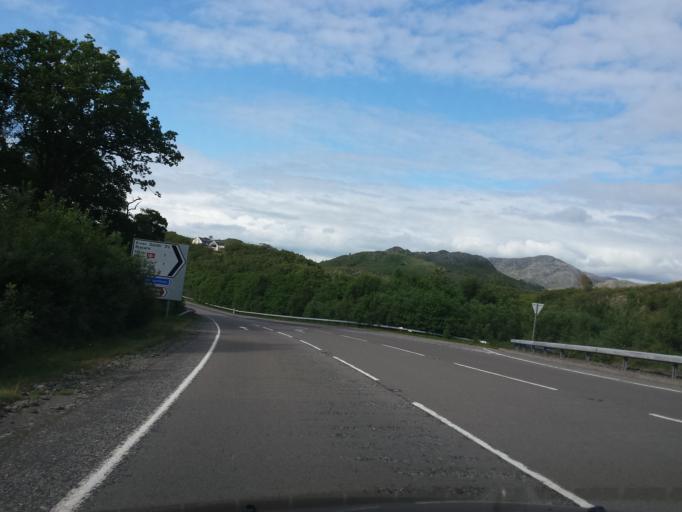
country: GB
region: Scotland
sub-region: Argyll and Bute
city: Isle Of Mull
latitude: 56.9597
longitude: -5.8192
